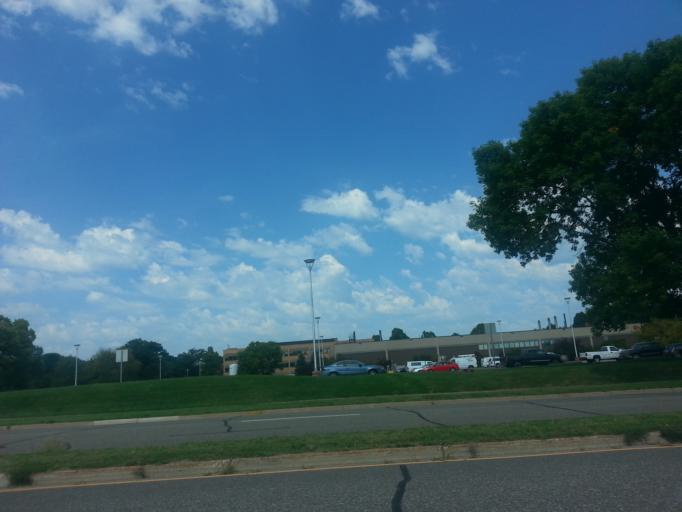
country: US
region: Minnesota
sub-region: Ramsey County
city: Maplewood
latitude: 44.9559
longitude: -92.9940
